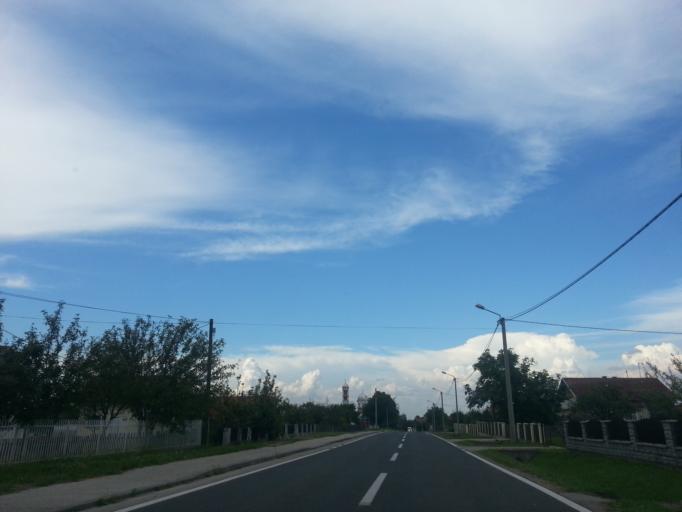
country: BA
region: Brcko
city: Brcko
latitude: 44.8310
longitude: 18.8194
